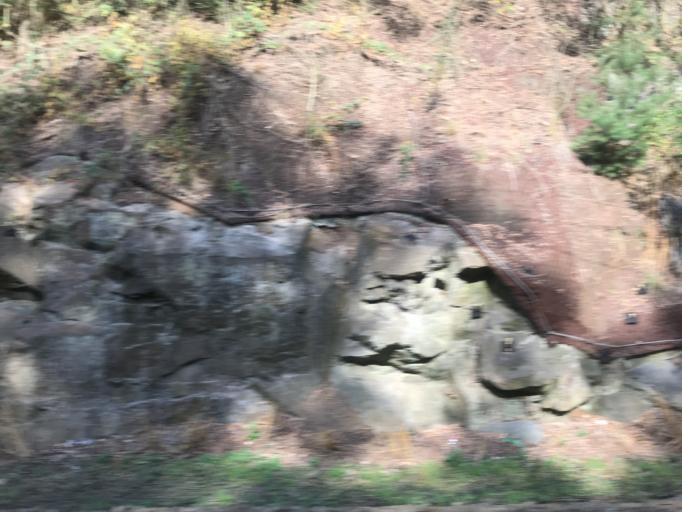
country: CZ
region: Central Bohemia
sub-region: Okres Benesov
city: Cercany
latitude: 49.8372
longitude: 14.6998
